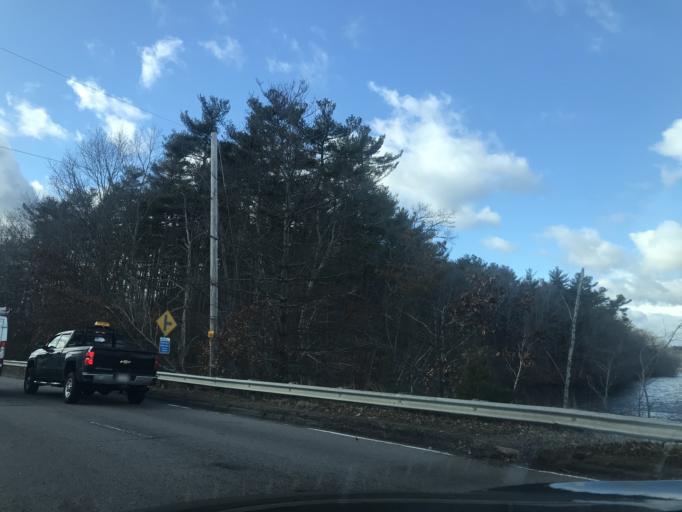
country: US
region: Massachusetts
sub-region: Plymouth County
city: Rockland
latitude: 42.1668
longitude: -70.8902
